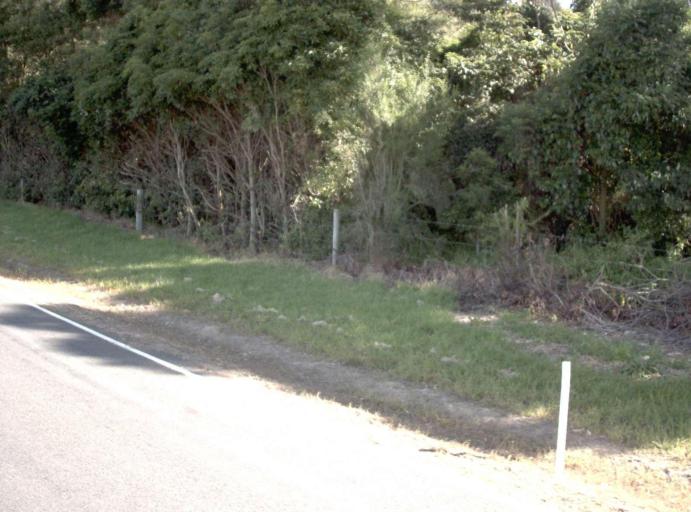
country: AU
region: Victoria
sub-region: East Gippsland
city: Lakes Entrance
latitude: -37.7531
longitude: 148.5225
